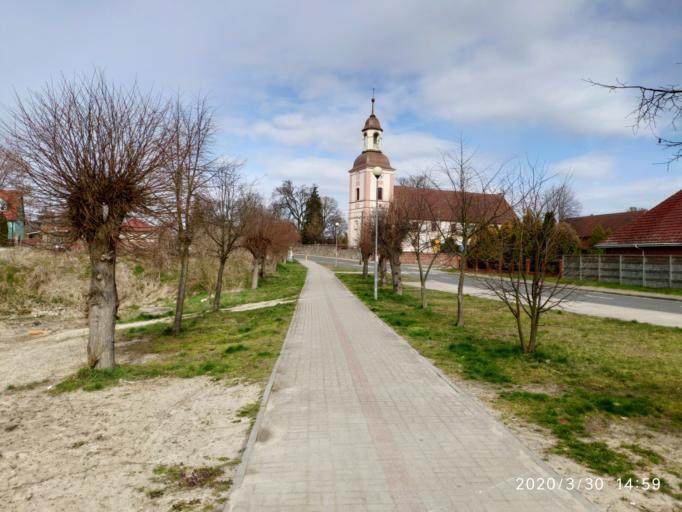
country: PL
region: Lubusz
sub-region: Powiat slubicki
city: Cybinka
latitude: 52.1927
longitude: 14.7912
